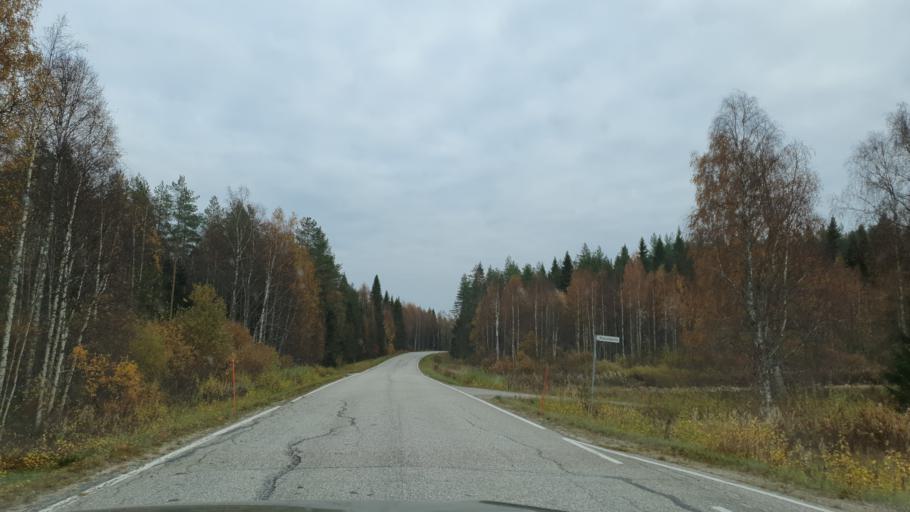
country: FI
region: Kainuu
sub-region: Kajaani
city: Ristijaervi
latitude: 64.4552
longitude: 28.3409
